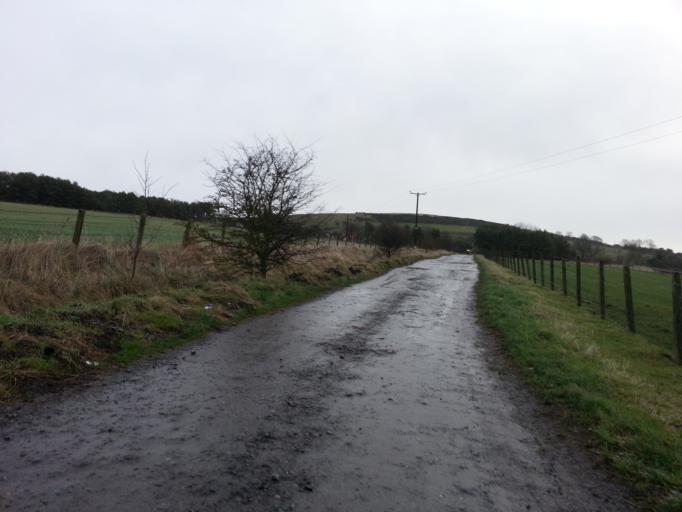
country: GB
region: England
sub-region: County Durham
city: Crook
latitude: 54.7266
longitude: -1.7485
